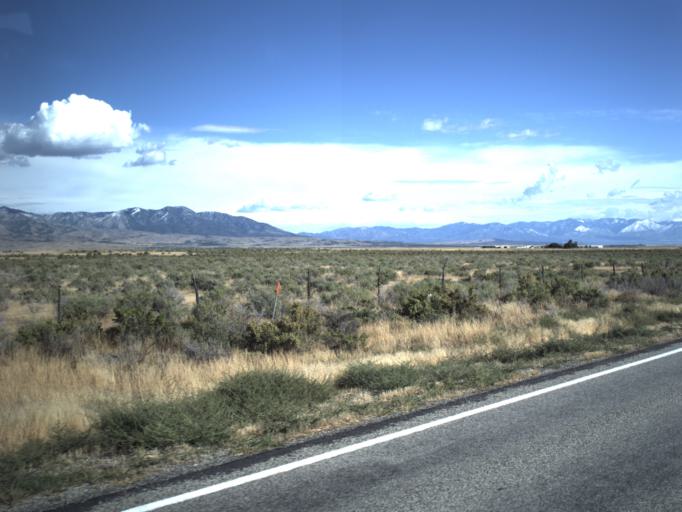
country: US
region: Utah
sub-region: Millard County
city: Delta
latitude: 39.3416
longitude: -112.4927
